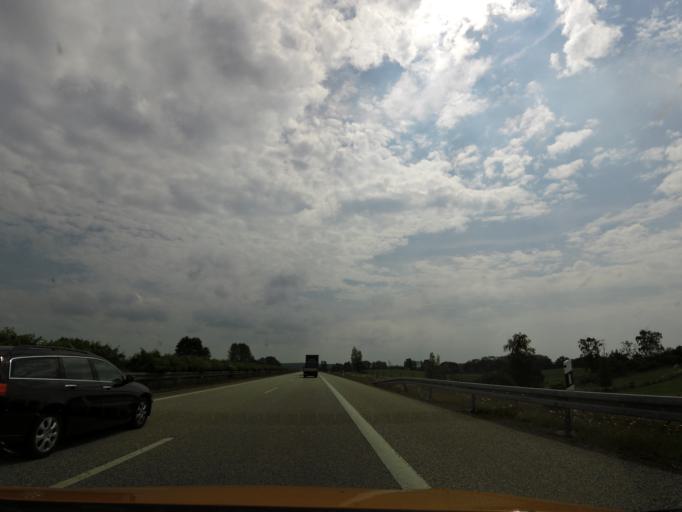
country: DE
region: Mecklenburg-Vorpommern
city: Leezen
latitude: 53.6790
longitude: 11.5090
